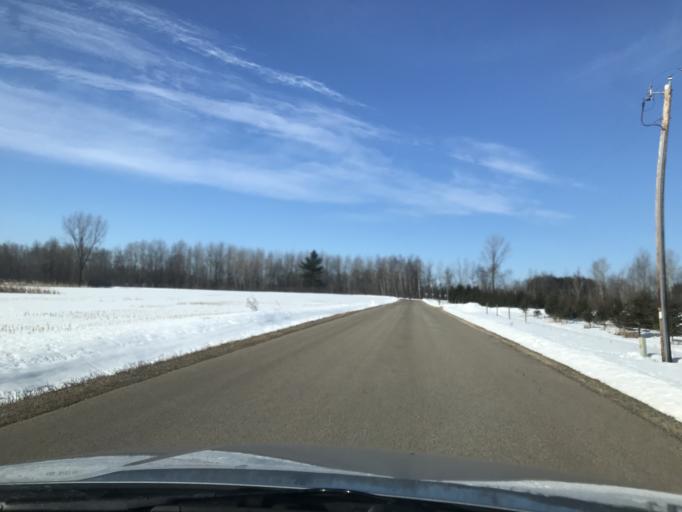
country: US
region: Wisconsin
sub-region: Oconto County
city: Oconto Falls
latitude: 44.9234
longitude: -88.1825
